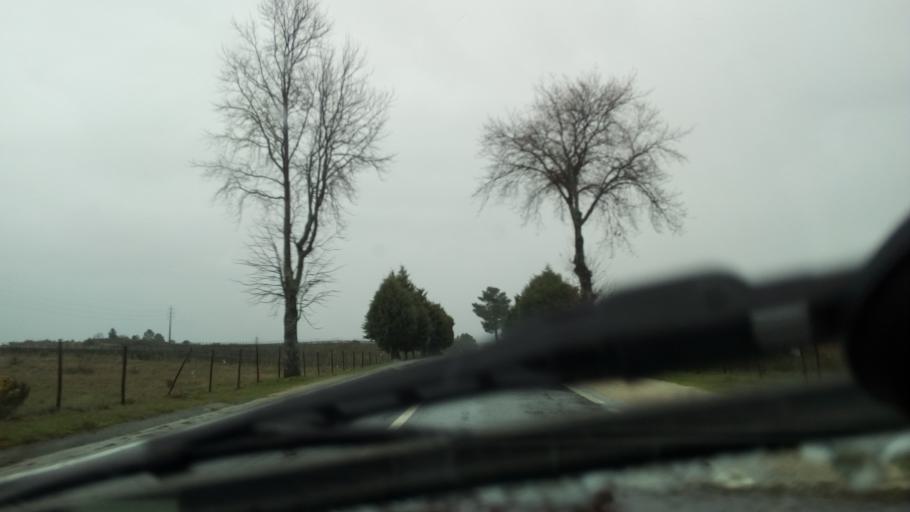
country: PT
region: Guarda
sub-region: Fornos de Algodres
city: Fornos de Algodres
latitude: 40.5378
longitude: -7.5442
